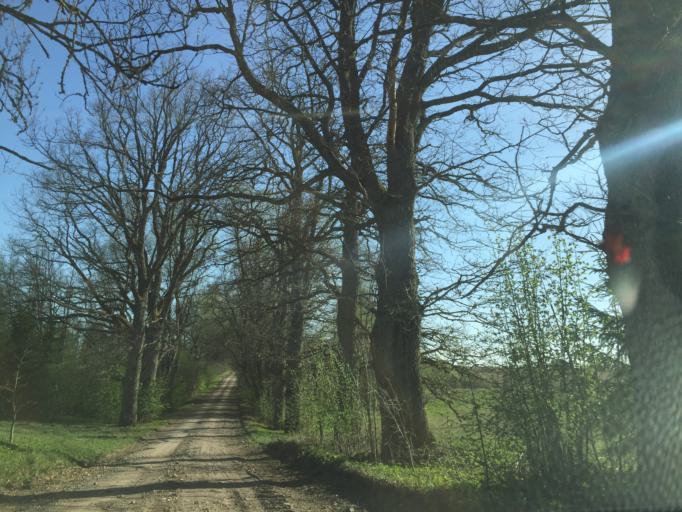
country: LV
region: Ergli
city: Ergli
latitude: 56.8764
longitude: 25.4837
